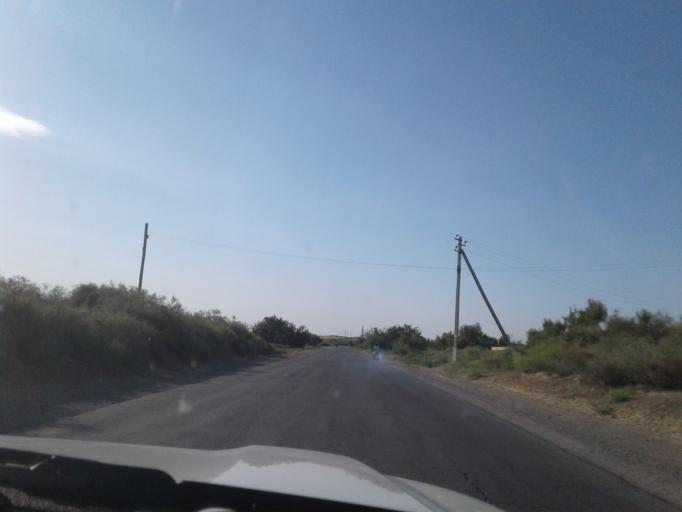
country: TM
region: Mary
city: Yoloeten
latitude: 37.0926
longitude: 62.4458
